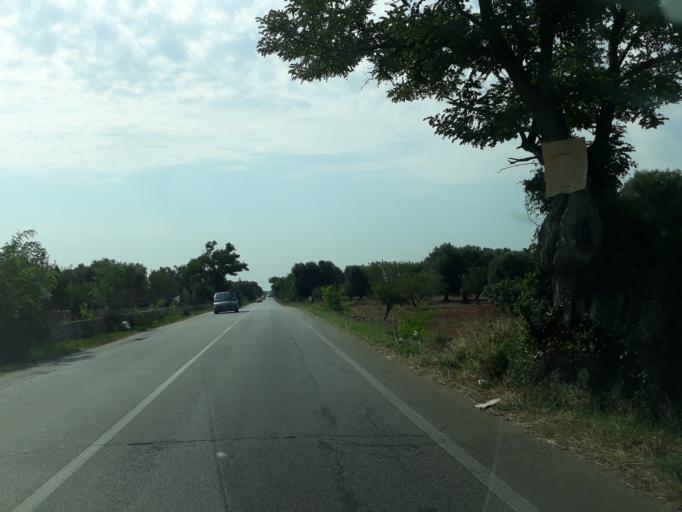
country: IT
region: Apulia
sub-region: Provincia di Brindisi
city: Carovigno
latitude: 40.6913
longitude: 17.6731
